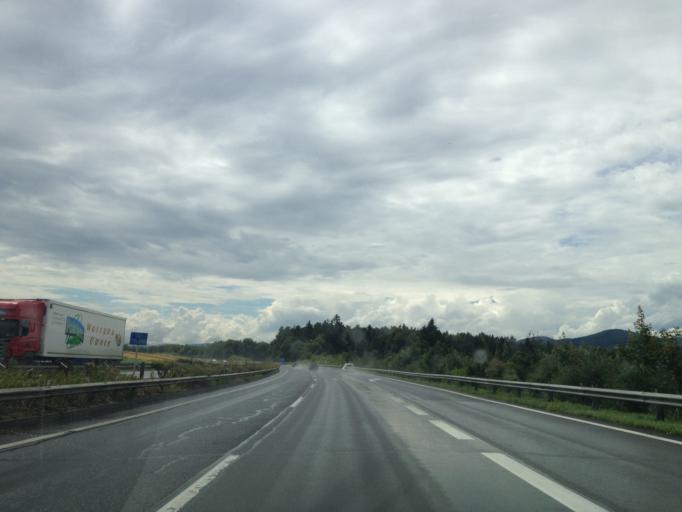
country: AT
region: Styria
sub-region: Politischer Bezirk Hartberg-Fuerstenfeld
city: Sankt Johann in der Haide
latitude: 47.2754
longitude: 16.0185
